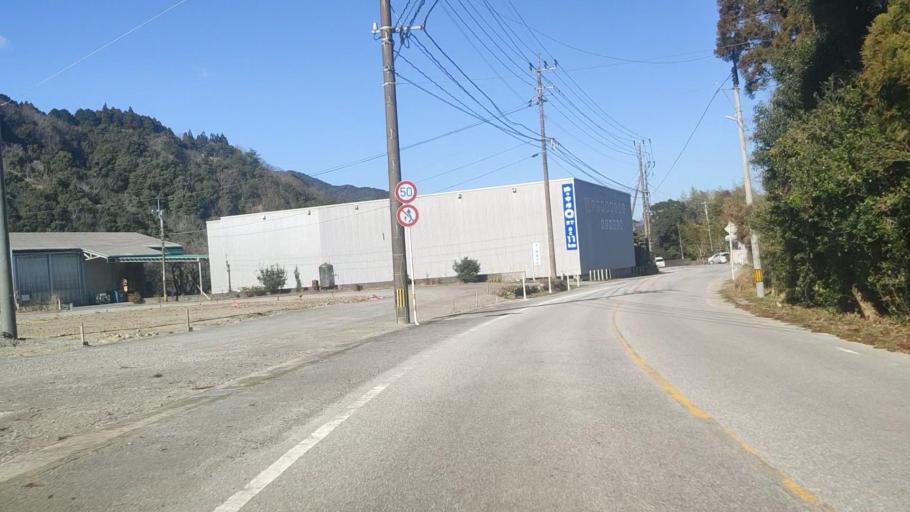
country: JP
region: Oita
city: Saiki
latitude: 32.9049
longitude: 131.9323
